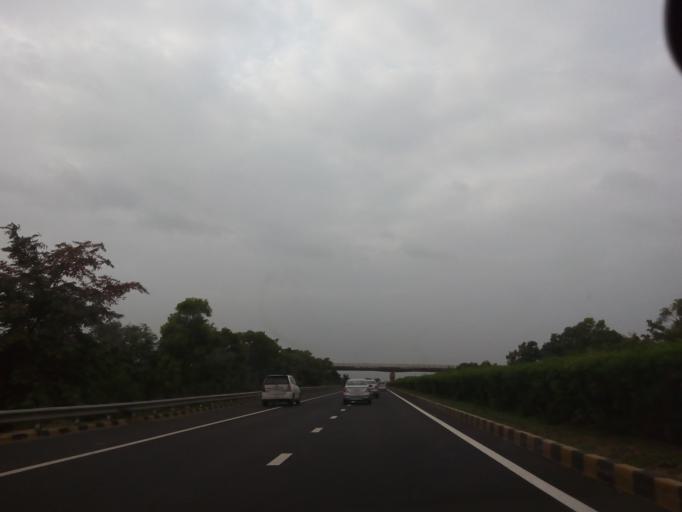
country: IN
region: Gujarat
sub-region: Kheda
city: Chaklasi
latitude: 22.6494
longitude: 72.9299
